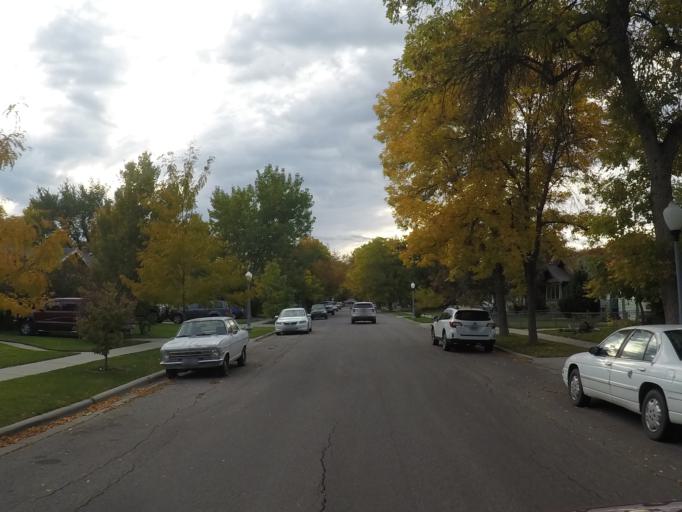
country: US
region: Montana
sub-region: Yellowstone County
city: Billings
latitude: 45.7821
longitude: -108.5258
